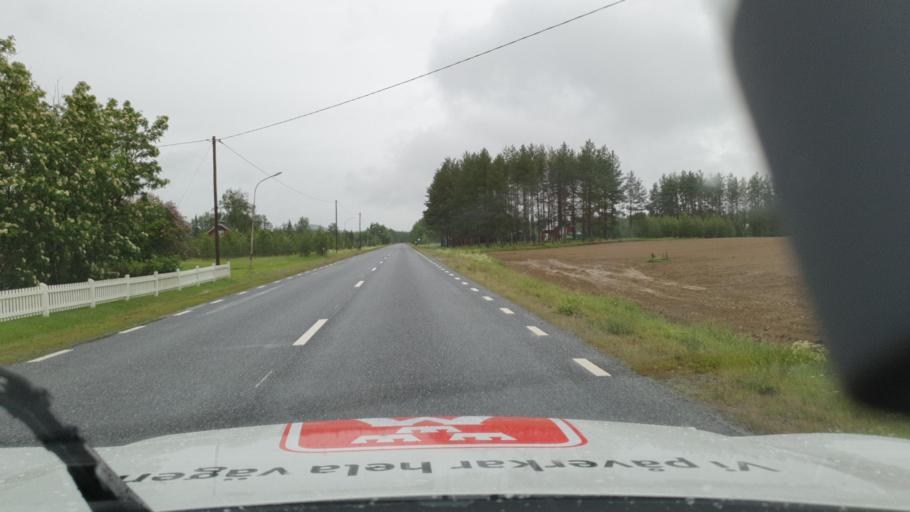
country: SE
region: Vaesterbotten
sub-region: Asele Kommun
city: Asele
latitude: 64.0358
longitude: 17.2949
